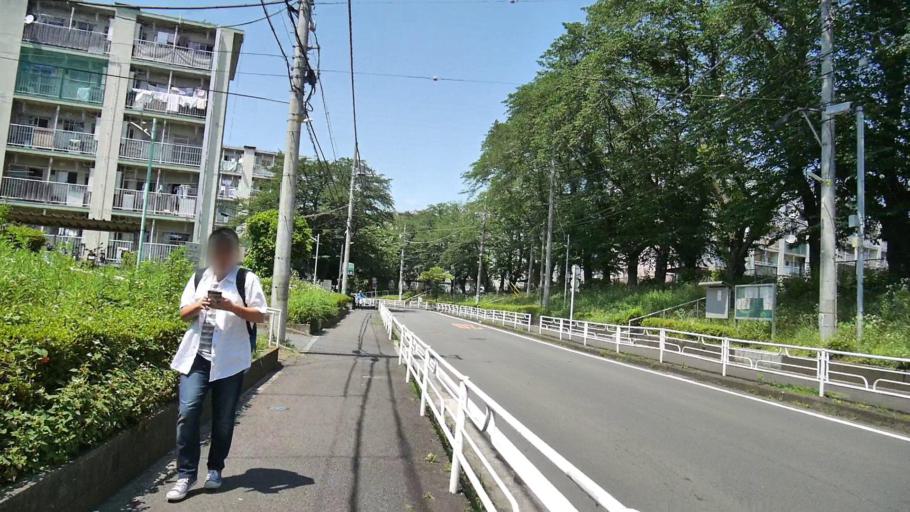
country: JP
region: Kanagawa
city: Fujisawa
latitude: 35.3997
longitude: 139.5190
